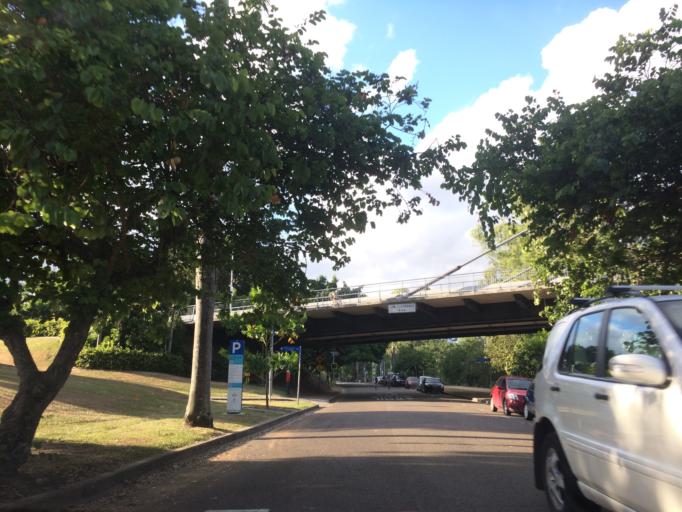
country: AU
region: Queensland
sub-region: Brisbane
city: Yeronga
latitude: -27.4984
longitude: 153.0194
